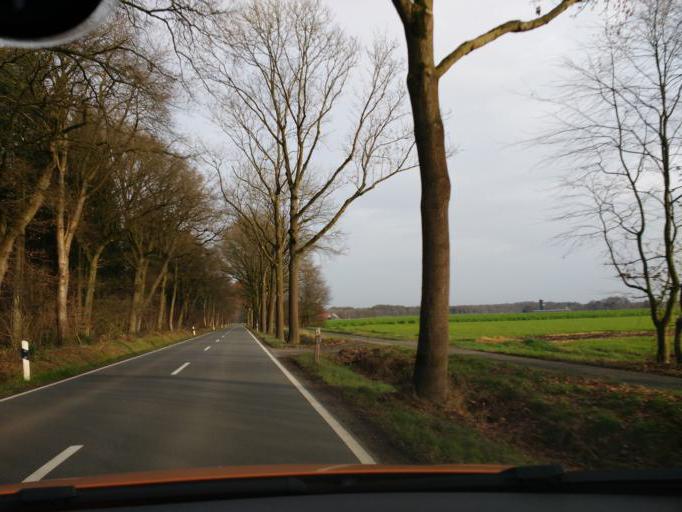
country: DE
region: Lower Saxony
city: Hude
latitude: 53.0520
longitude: 8.4525
